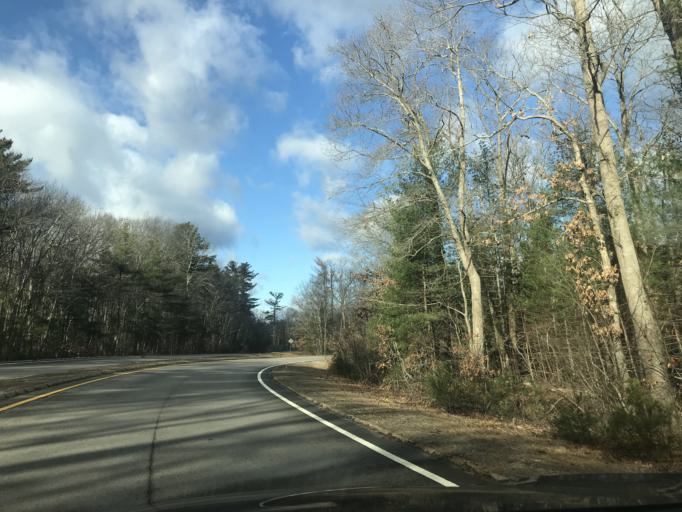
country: US
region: Massachusetts
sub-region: Plymouth County
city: Hanover
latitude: 42.1501
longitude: -70.8477
